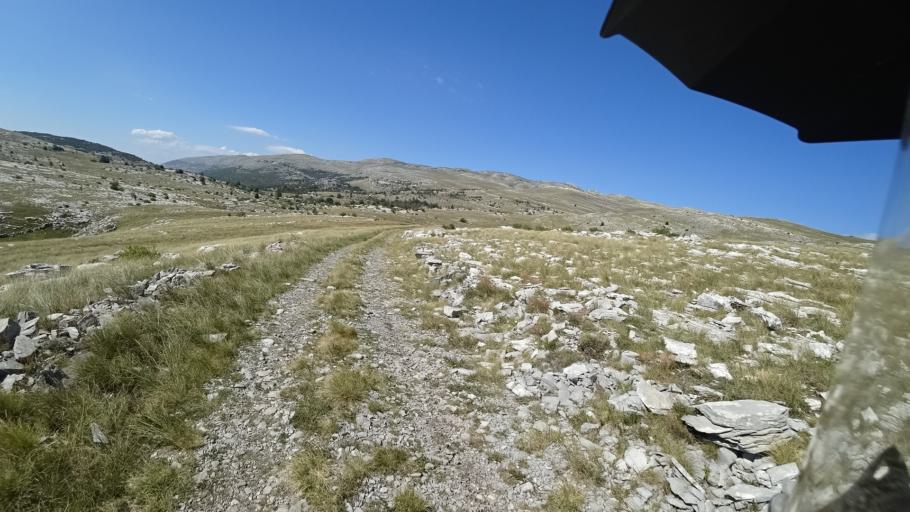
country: HR
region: Splitsko-Dalmatinska
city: Hrvace
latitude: 43.9004
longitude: 16.5964
